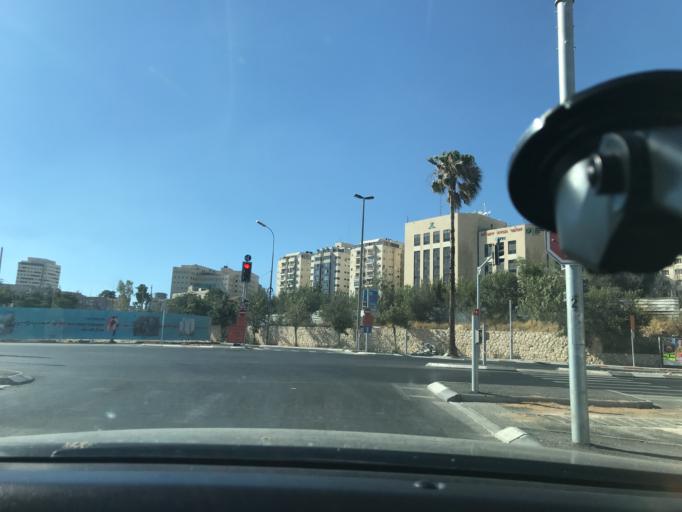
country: IL
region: Jerusalem
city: West Jerusalem
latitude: 31.7861
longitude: 35.2073
